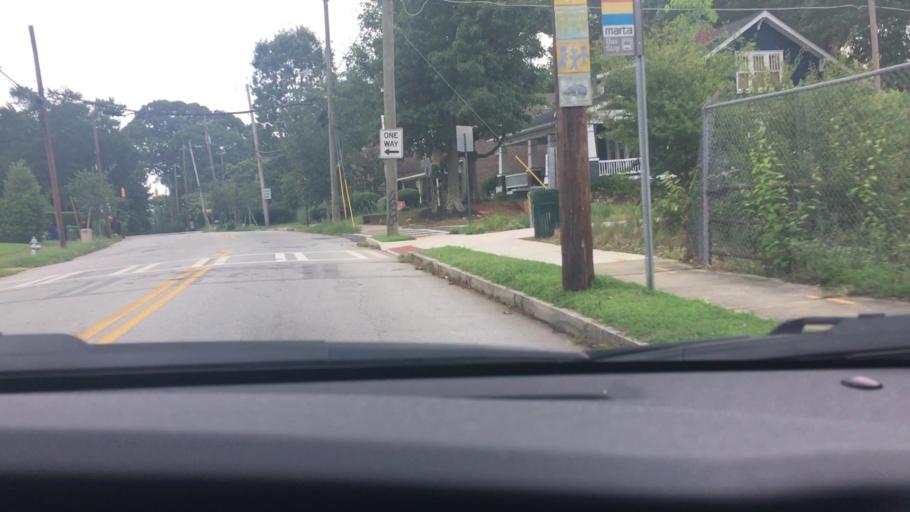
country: US
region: Georgia
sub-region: Fulton County
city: Atlanta
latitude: 33.7424
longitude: -84.4339
